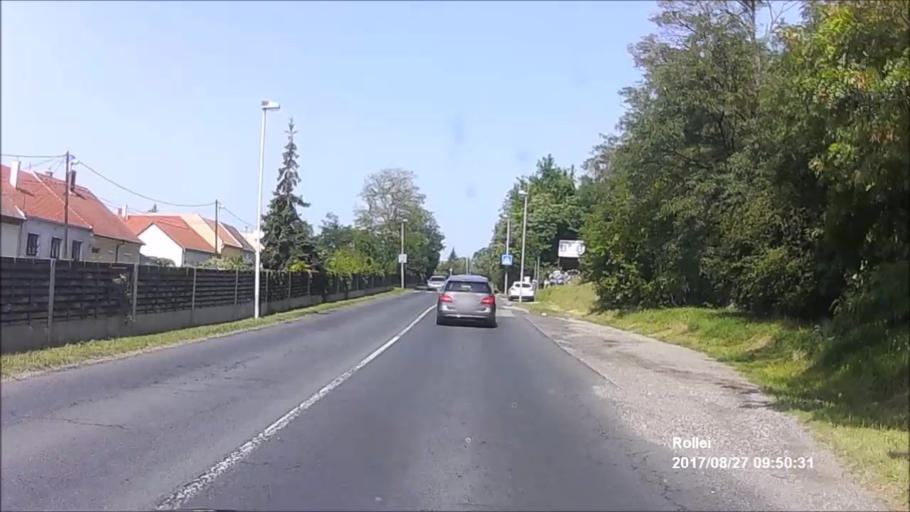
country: HU
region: Gyor-Moson-Sopron
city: Sopron
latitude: 47.6941
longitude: 16.5868
